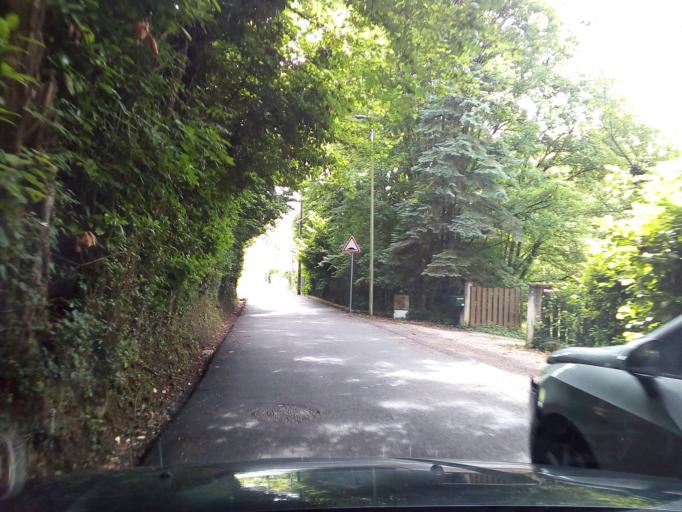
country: FR
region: Rhone-Alpes
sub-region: Departement de l'Isere
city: Gieres
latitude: 45.1711
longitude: 5.7811
